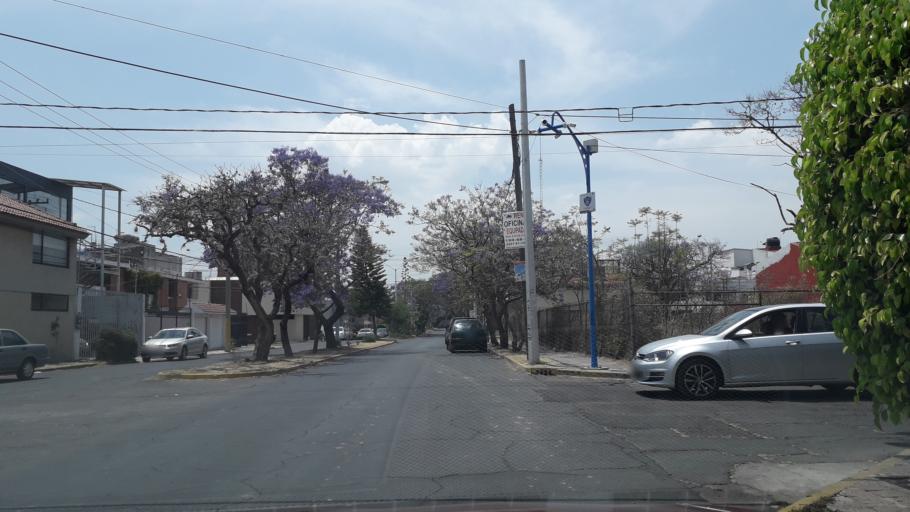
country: MX
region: Puebla
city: Puebla
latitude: 19.0219
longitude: -98.1946
